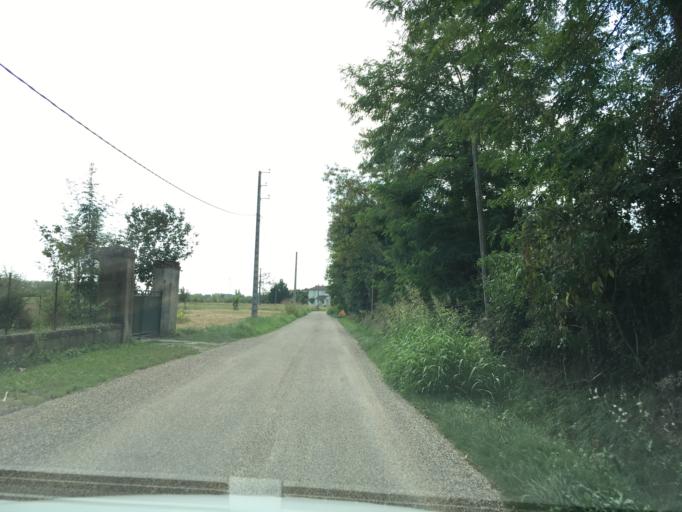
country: FR
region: Midi-Pyrenees
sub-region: Departement du Tarn-et-Garonne
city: Montbeton
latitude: 44.0142
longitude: 1.3137
